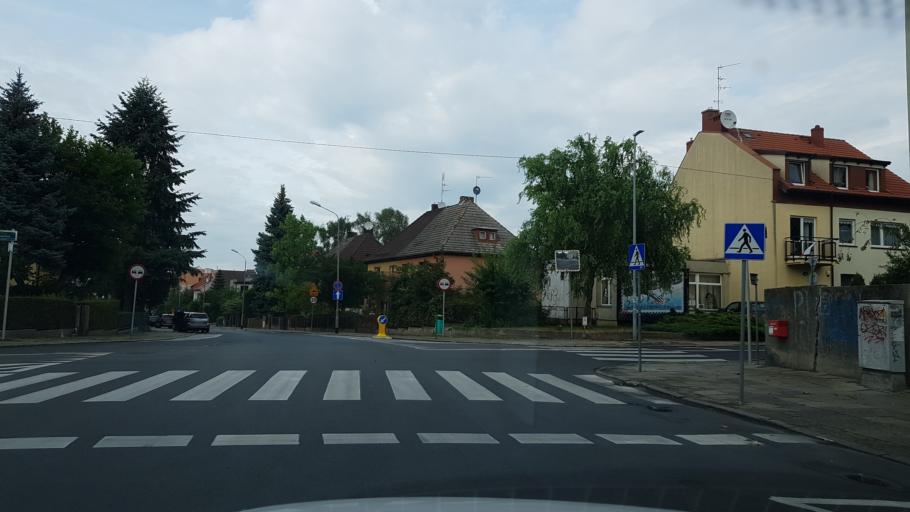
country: PL
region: West Pomeranian Voivodeship
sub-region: Szczecin
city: Szczecin
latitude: 53.4359
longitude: 14.5016
